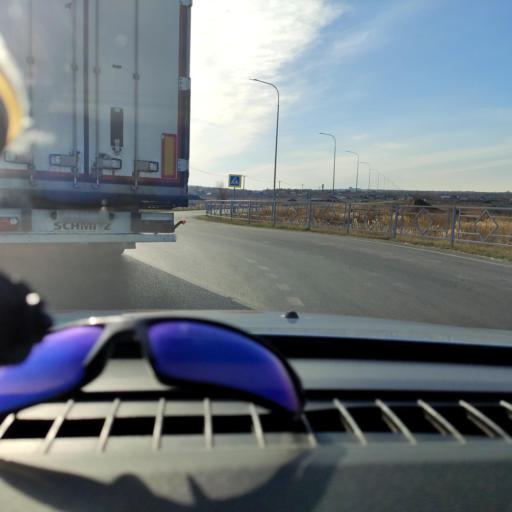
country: RU
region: Samara
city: Samara
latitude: 53.0909
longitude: 50.1346
